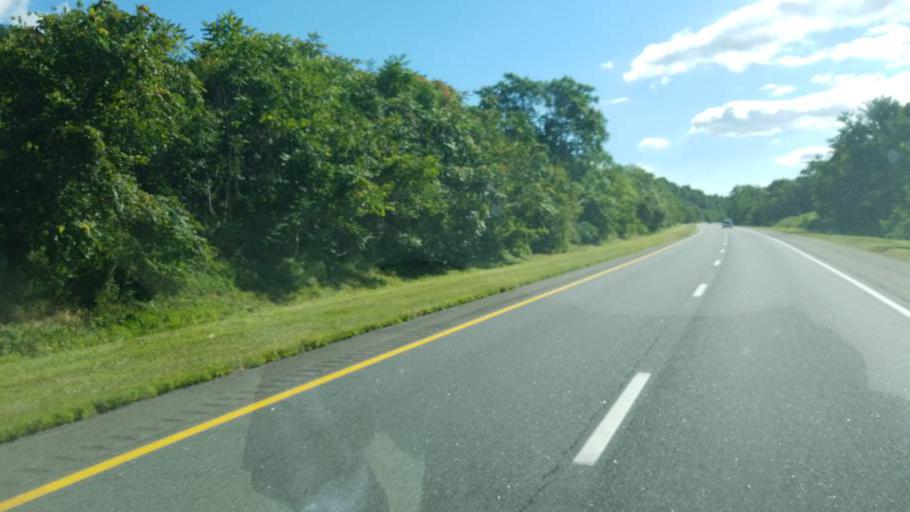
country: US
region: Virginia
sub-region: Warren County
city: Shenandoah Farms
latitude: 38.9079
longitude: -77.9861
